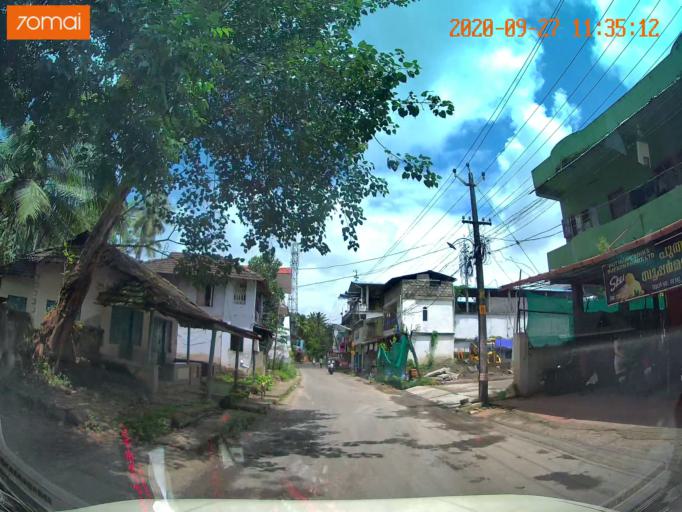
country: IN
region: Kerala
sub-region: Thrissur District
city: Thanniyam
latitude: 10.4422
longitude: 76.1257
